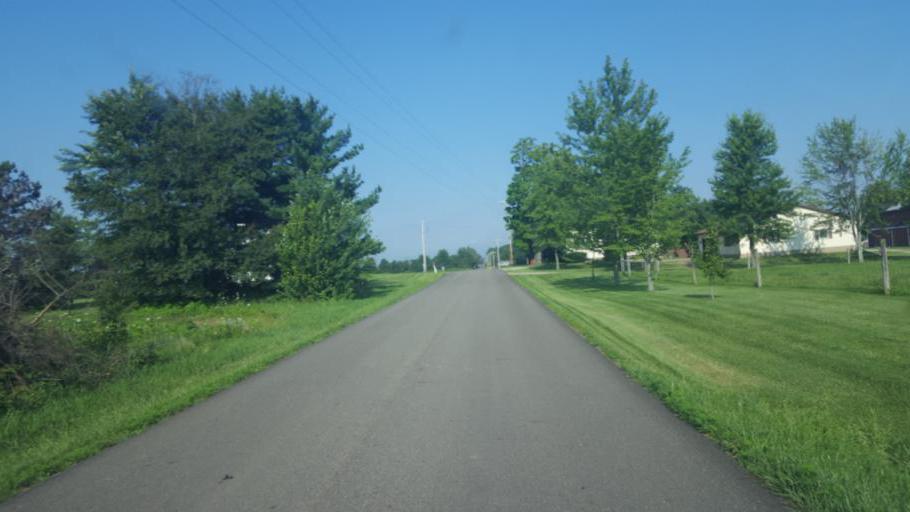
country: US
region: Ohio
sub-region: Crawford County
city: Galion
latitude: 40.6239
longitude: -82.7138
